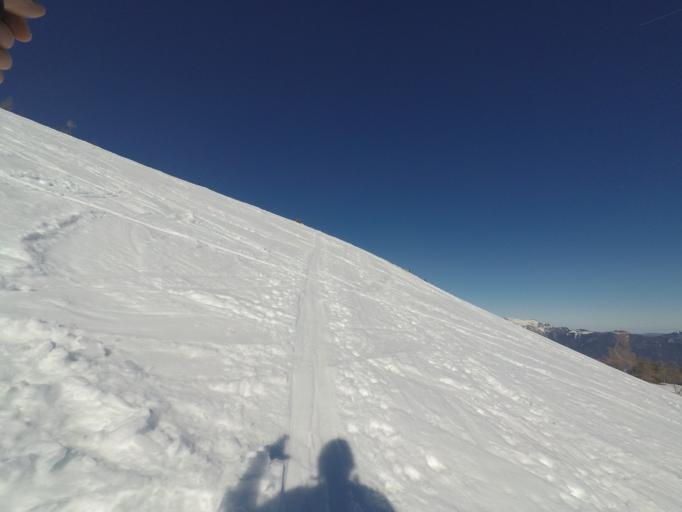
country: AT
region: Upper Austria
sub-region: Politischer Bezirk Gmunden
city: Sankt Wolfgang im Salzkammergut
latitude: 47.6662
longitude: 13.3779
